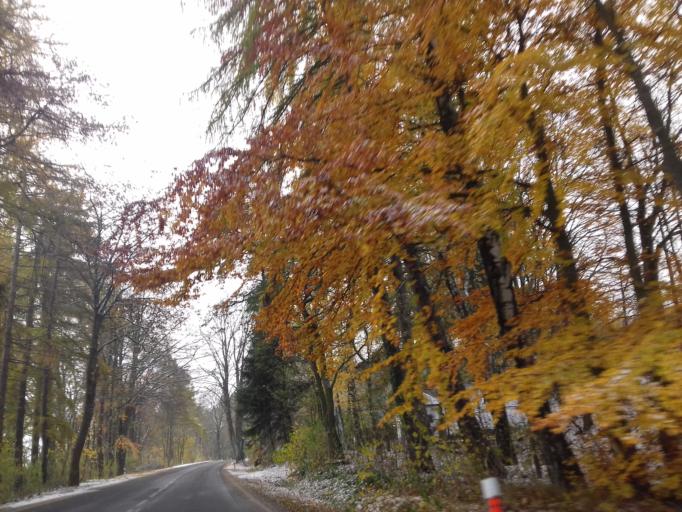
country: CZ
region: Plzensky
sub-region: Okres Domazlice
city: Klenci pod Cerchovem
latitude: 49.4284
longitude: 12.8122
